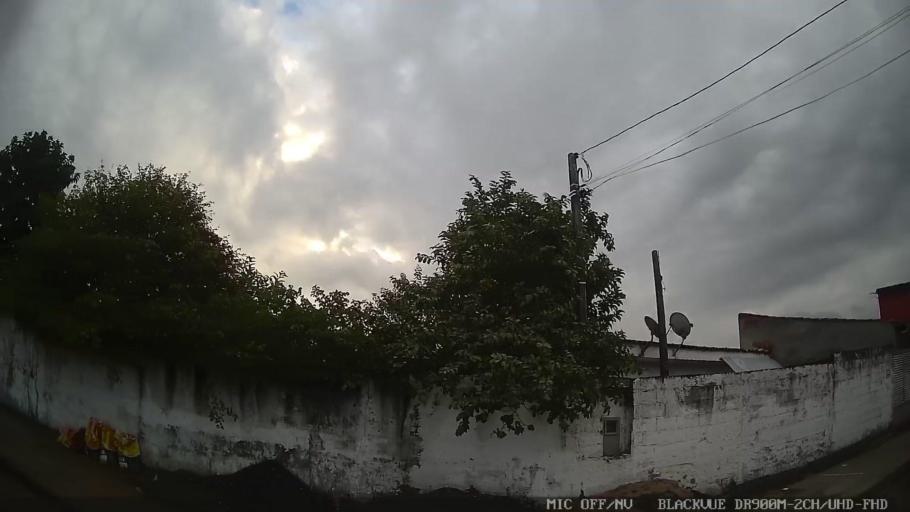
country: BR
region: Sao Paulo
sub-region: Itanhaem
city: Itanhaem
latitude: -24.1789
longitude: -46.7917
